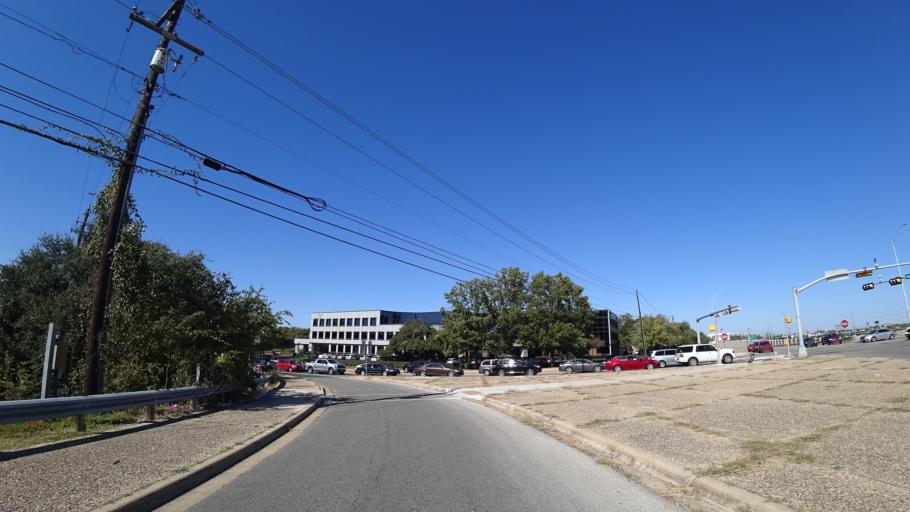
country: US
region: Texas
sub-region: Travis County
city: West Lake Hills
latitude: 30.3609
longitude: -97.7456
